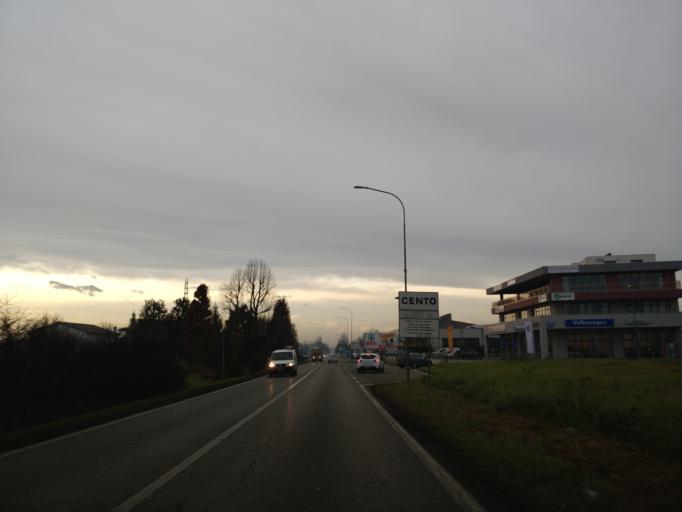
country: IT
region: Emilia-Romagna
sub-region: Provincia di Ferrara
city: Corpo Reno
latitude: 44.7483
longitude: 11.2987
